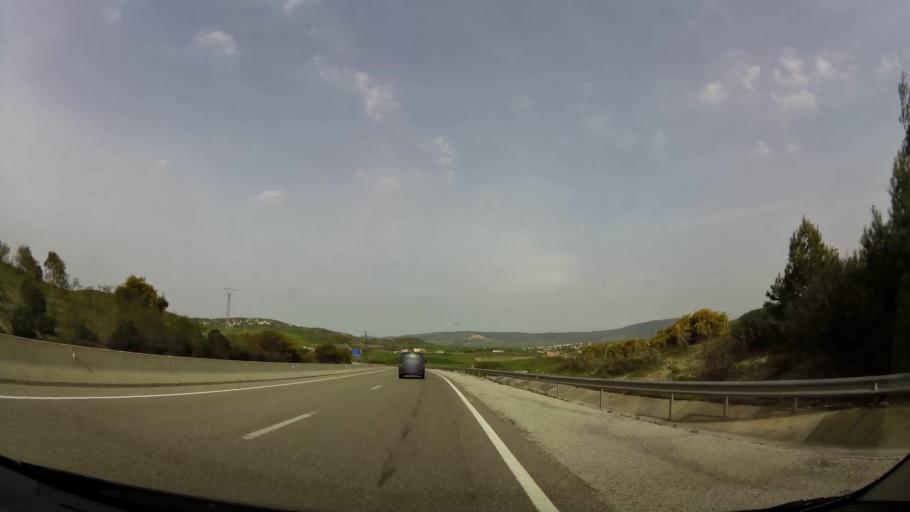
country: MA
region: Tanger-Tetouan
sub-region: Tanger-Assilah
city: Tangier
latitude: 35.6804
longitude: -5.7270
